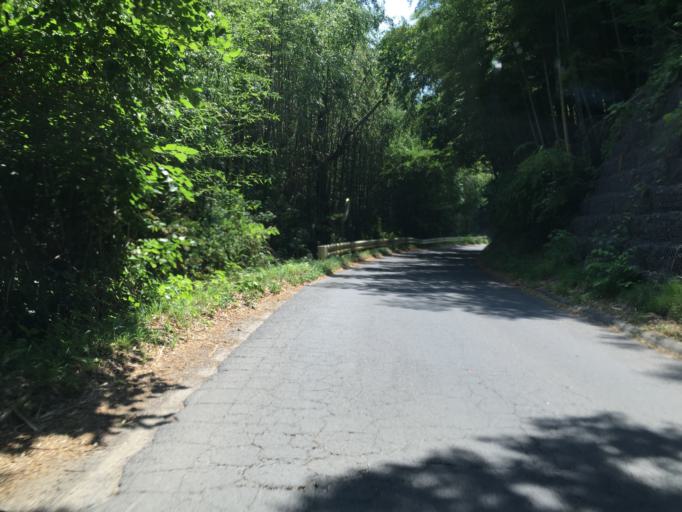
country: JP
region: Fukushima
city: Yanagawamachi-saiwaicho
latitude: 37.9045
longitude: 140.6603
